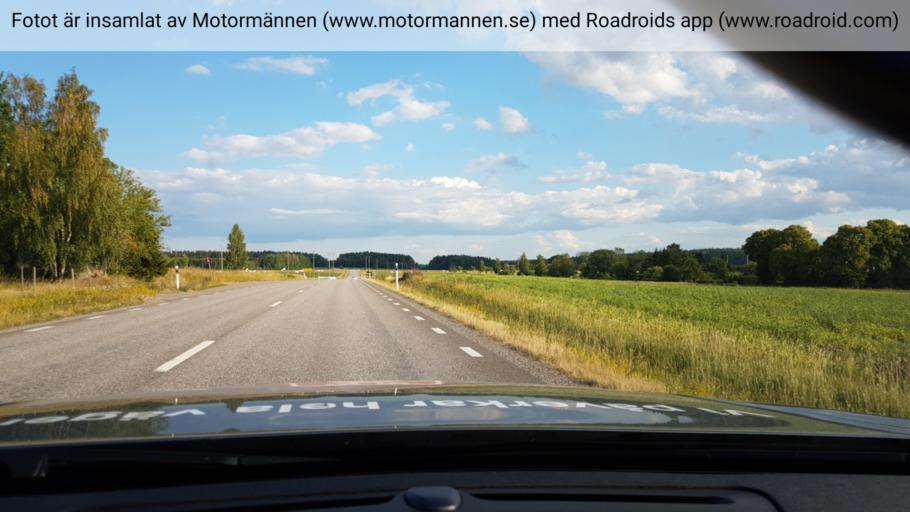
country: SE
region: Uppsala
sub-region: Heby Kommun
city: Heby
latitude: 59.9242
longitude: 16.8797
